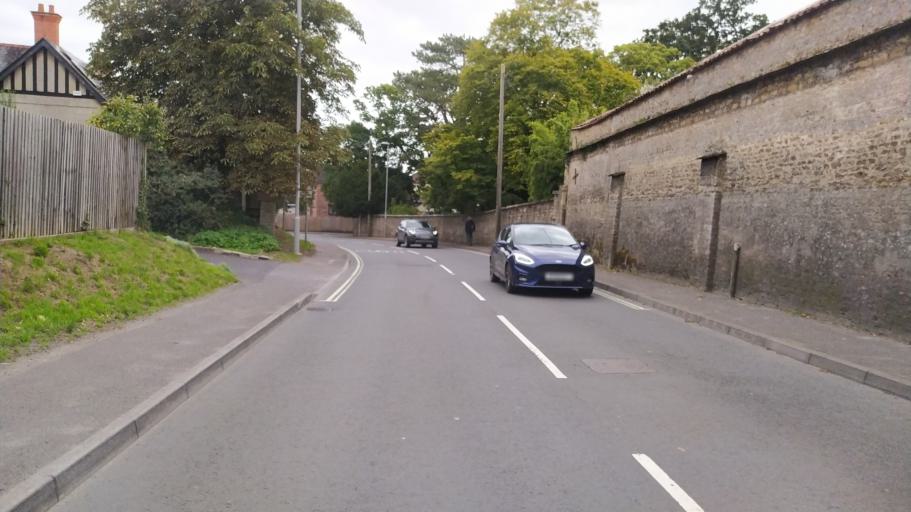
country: GB
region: England
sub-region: Dorset
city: Gillingham
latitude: 51.0376
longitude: -2.2818
